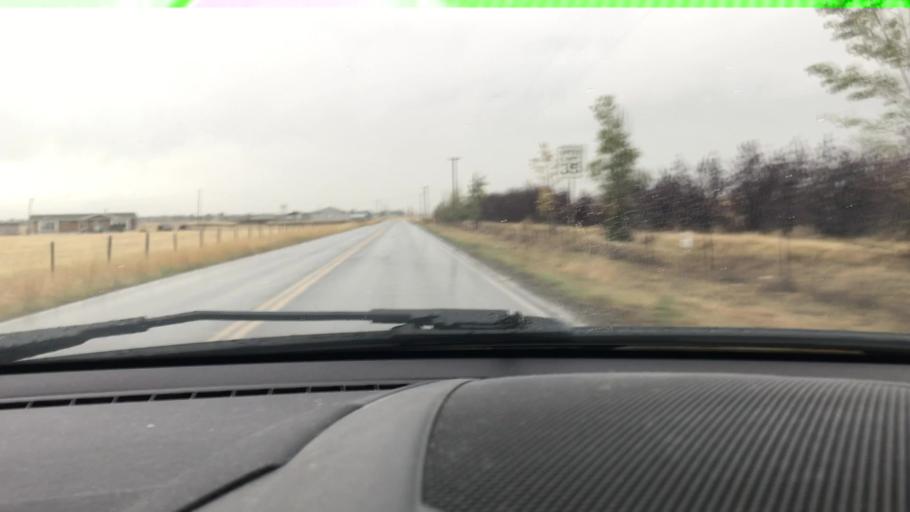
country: US
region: Montana
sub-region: Gallatin County
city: Belgrade
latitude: 45.7513
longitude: -111.1646
